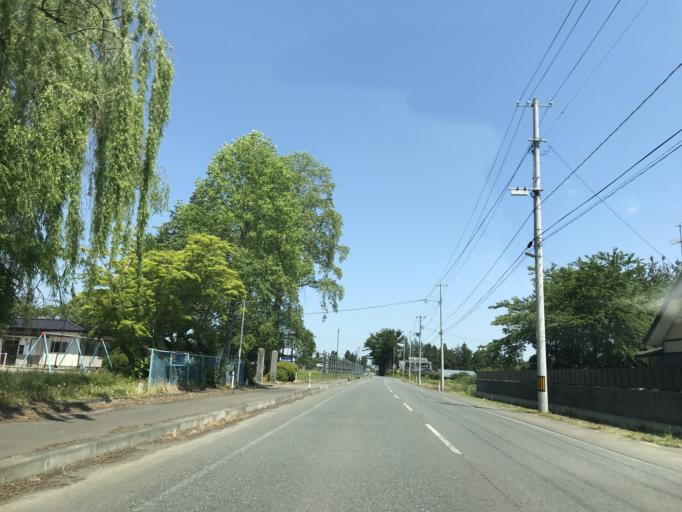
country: JP
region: Iwate
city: Kitakami
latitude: 39.2421
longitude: 141.0666
